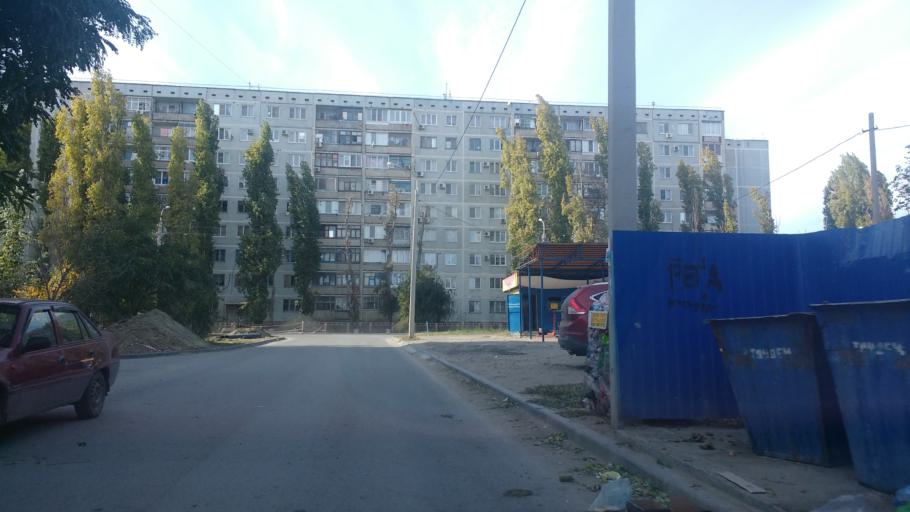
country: RU
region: Volgograd
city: Krasnoslobodsk
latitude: 48.7653
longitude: 44.5480
